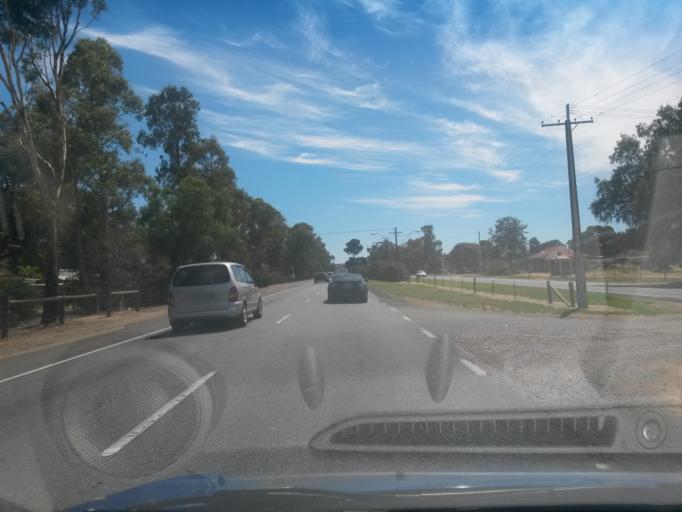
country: AU
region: South Australia
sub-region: Salisbury
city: Salisbury
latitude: -34.7790
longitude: 138.6580
